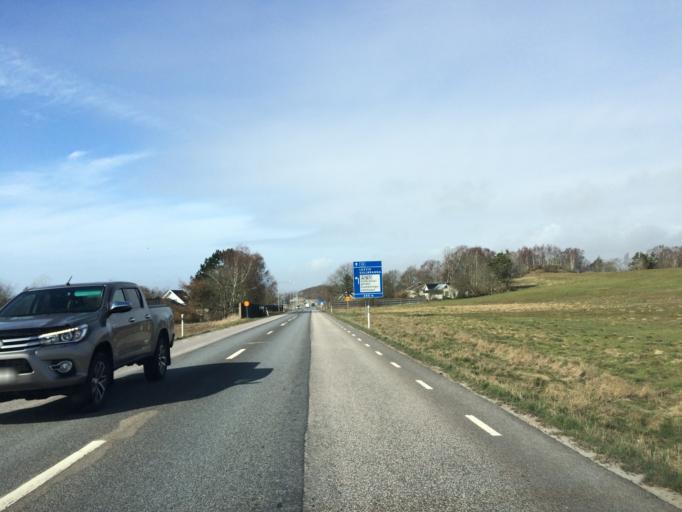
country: SE
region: Halland
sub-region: Halmstads Kommun
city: Paarp
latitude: 56.5936
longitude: 12.9789
